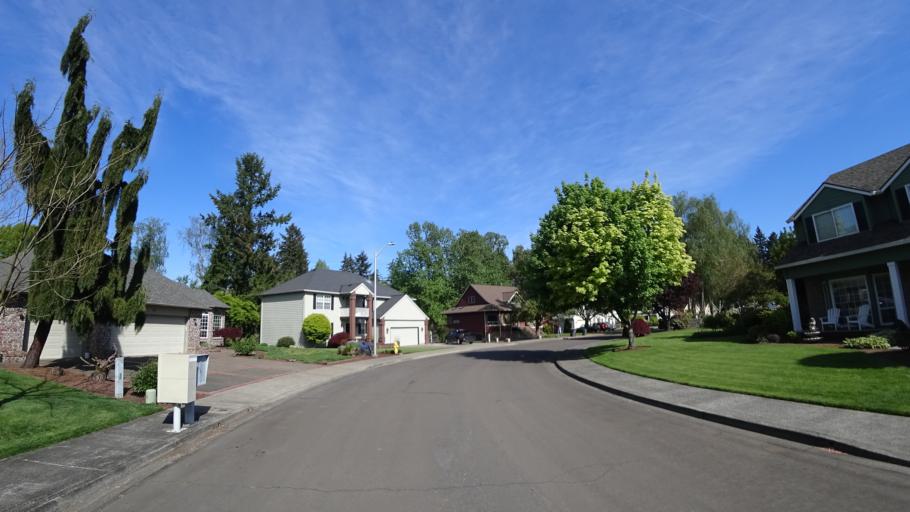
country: US
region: Oregon
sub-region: Washington County
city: Hillsboro
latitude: 45.5196
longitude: -122.9618
